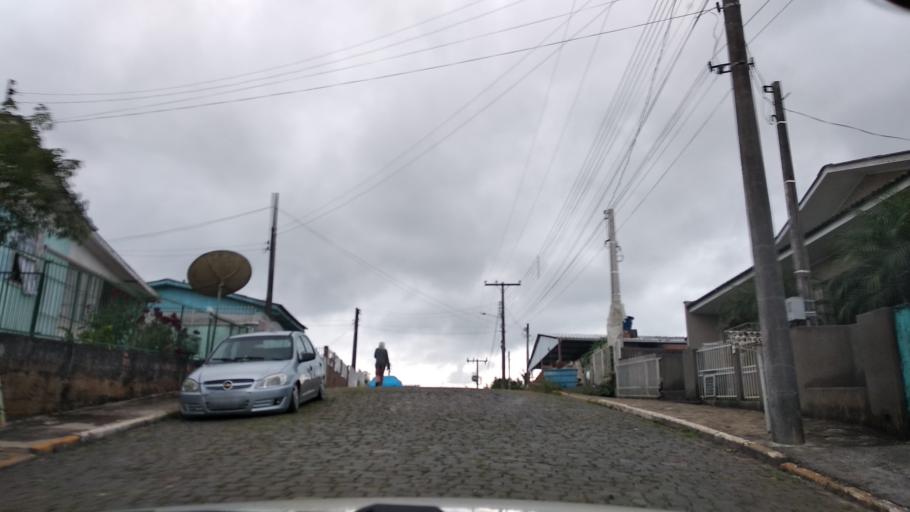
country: BR
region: Santa Catarina
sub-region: Videira
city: Videira
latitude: -26.9872
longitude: -51.1724
